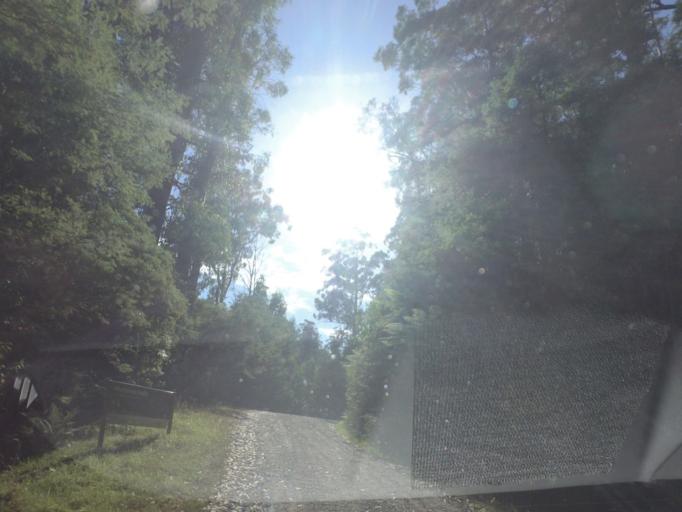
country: AU
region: Victoria
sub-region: Yarra Ranges
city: Millgrove
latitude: -37.5012
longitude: 145.8247
